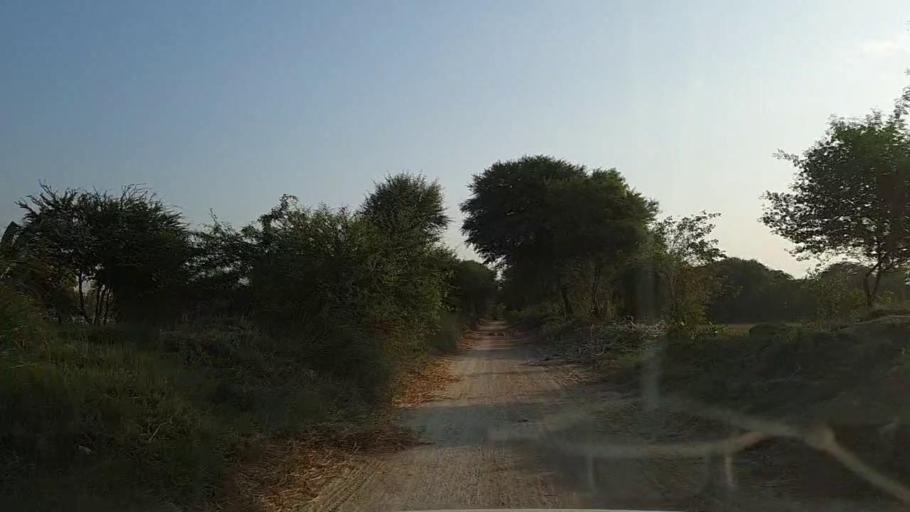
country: PK
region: Sindh
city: Daro Mehar
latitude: 24.7728
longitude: 68.1935
